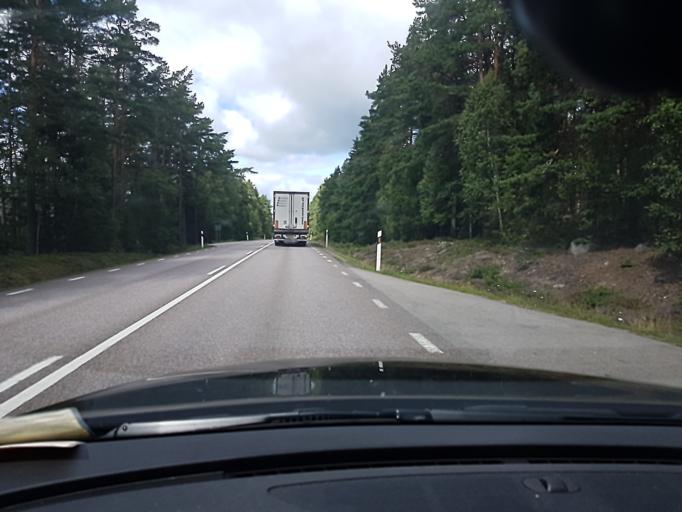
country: SE
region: Kronoberg
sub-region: Lessebo Kommun
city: Hovmantorp
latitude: 56.7878
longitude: 15.1472
